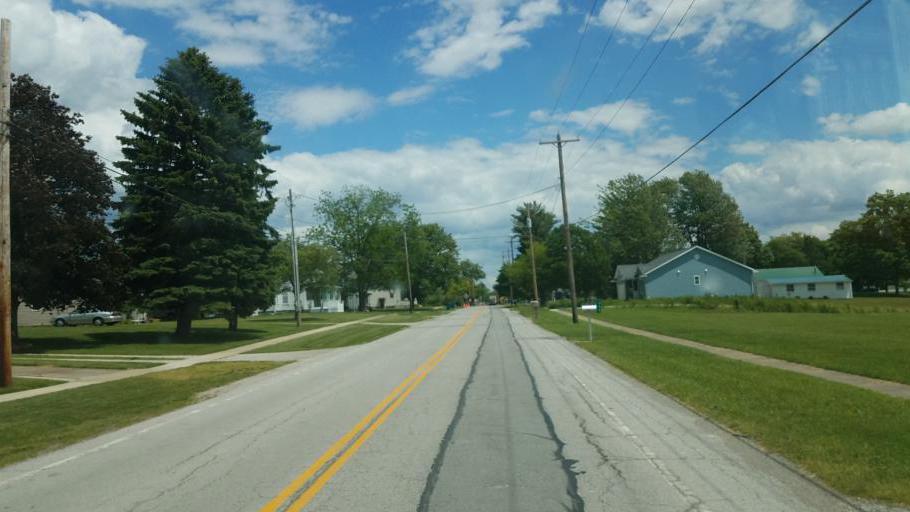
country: US
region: Ohio
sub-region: Huron County
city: Monroeville
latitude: 41.2416
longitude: -82.7118
